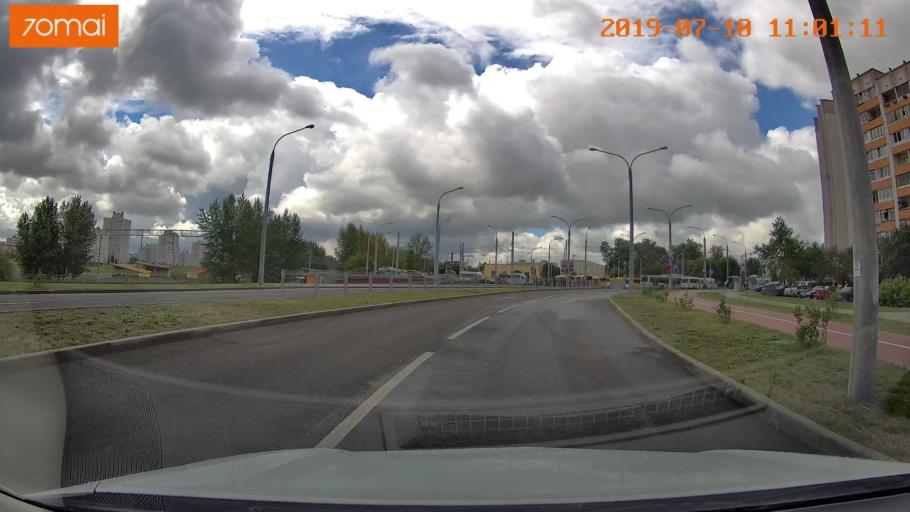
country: BY
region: Minsk
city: Syenitsa
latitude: 53.8524
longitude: 27.5557
